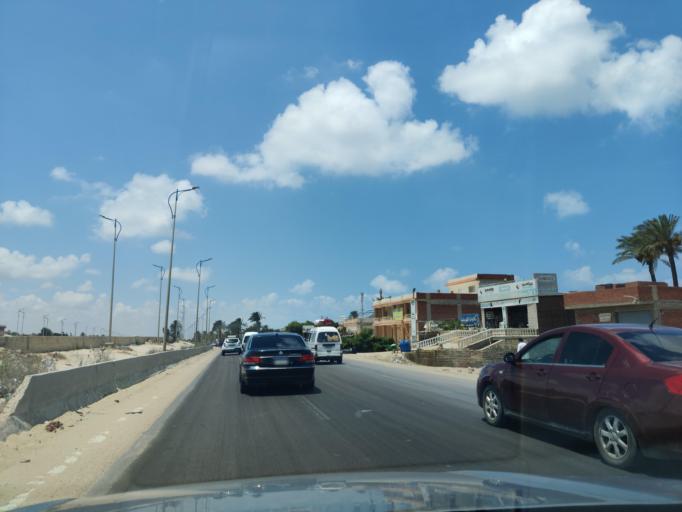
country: EG
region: Alexandria
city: Alexandria
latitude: 31.0080
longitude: 29.6216
